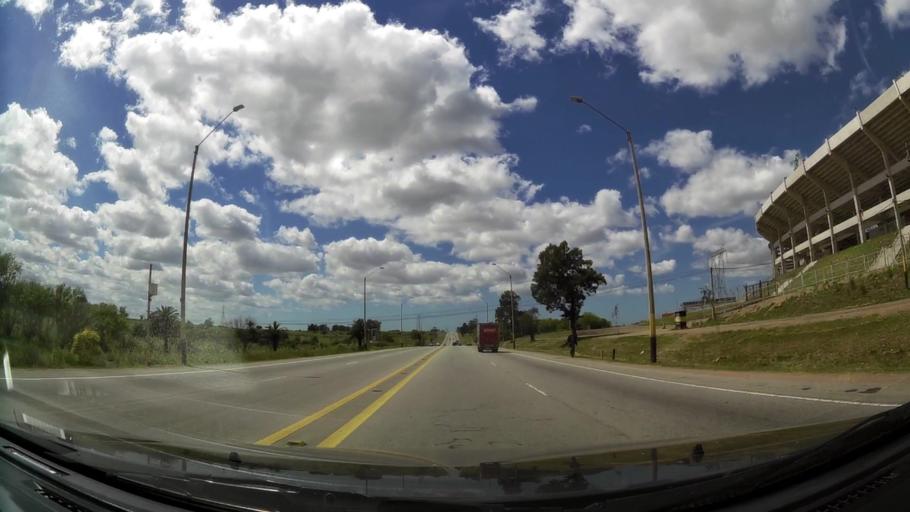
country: UY
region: Canelones
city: Colonia Nicolich
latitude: -34.7958
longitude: -56.0664
